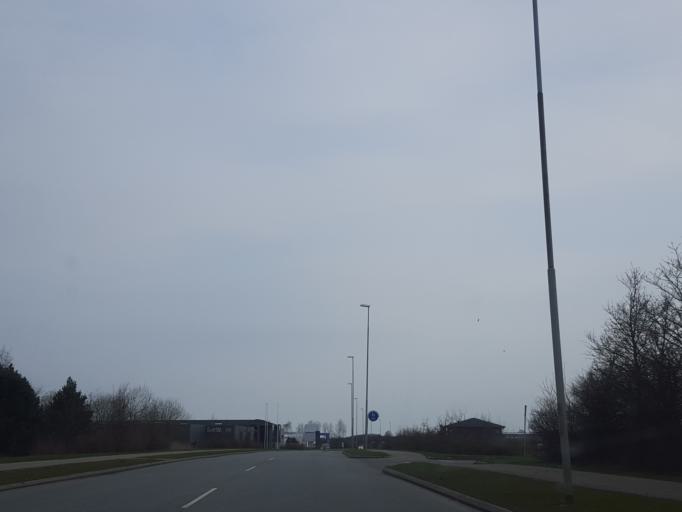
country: DK
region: South Denmark
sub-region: Esbjerg Kommune
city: Esbjerg
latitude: 55.5127
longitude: 8.4669
